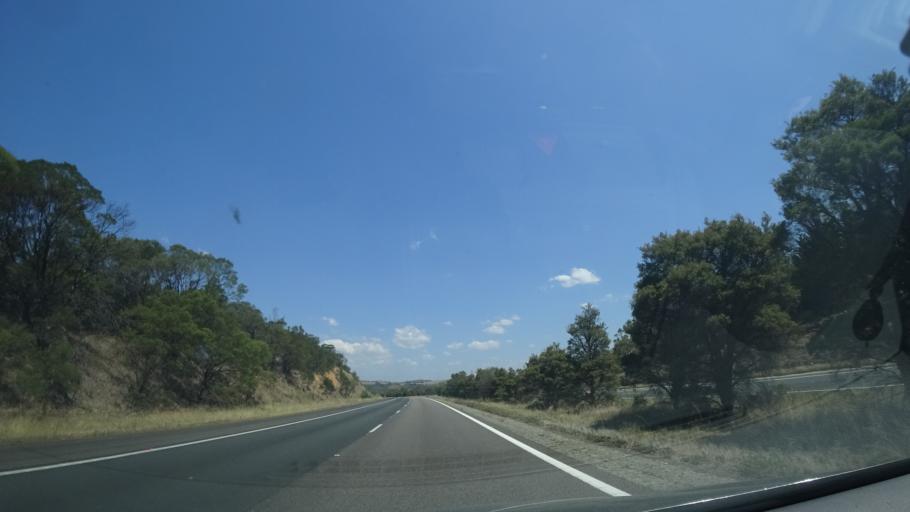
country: AU
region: New South Wales
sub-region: Wingecarribee
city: Bundanoon
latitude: -34.5618
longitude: 150.2566
